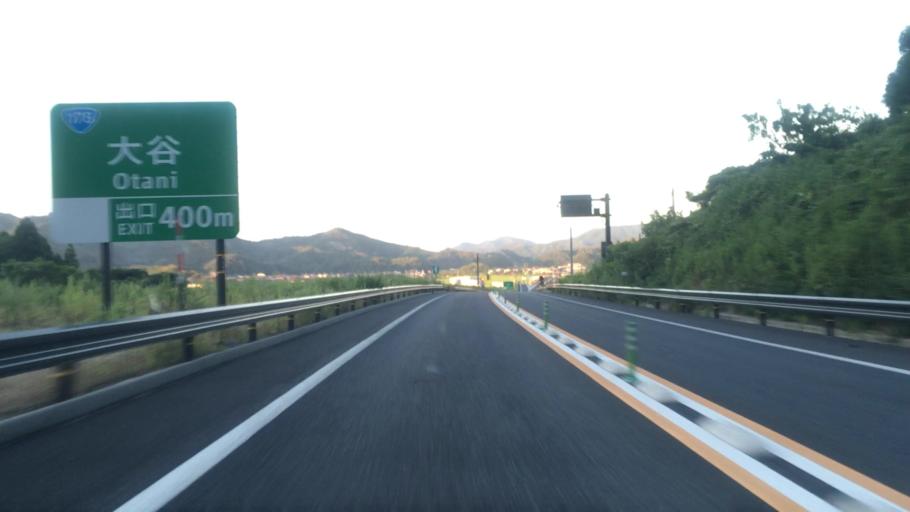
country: JP
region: Tottori
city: Tottori
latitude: 35.5677
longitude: 134.2924
